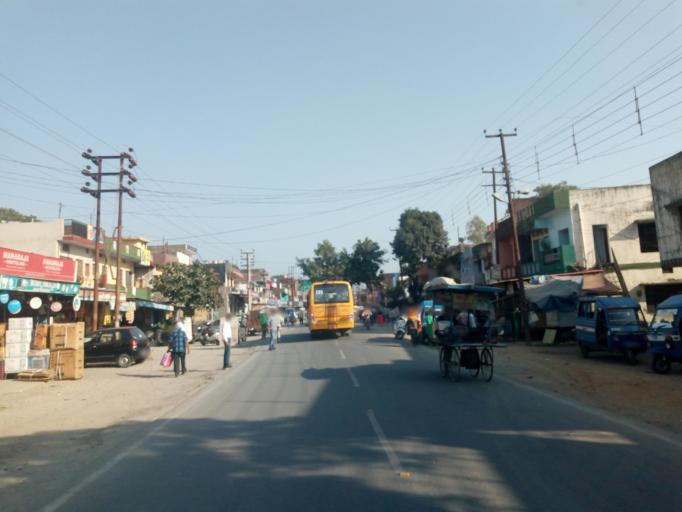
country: IN
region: Uttarakhand
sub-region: Dehradun
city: Harbatpur
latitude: 30.4397
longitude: 77.7353
